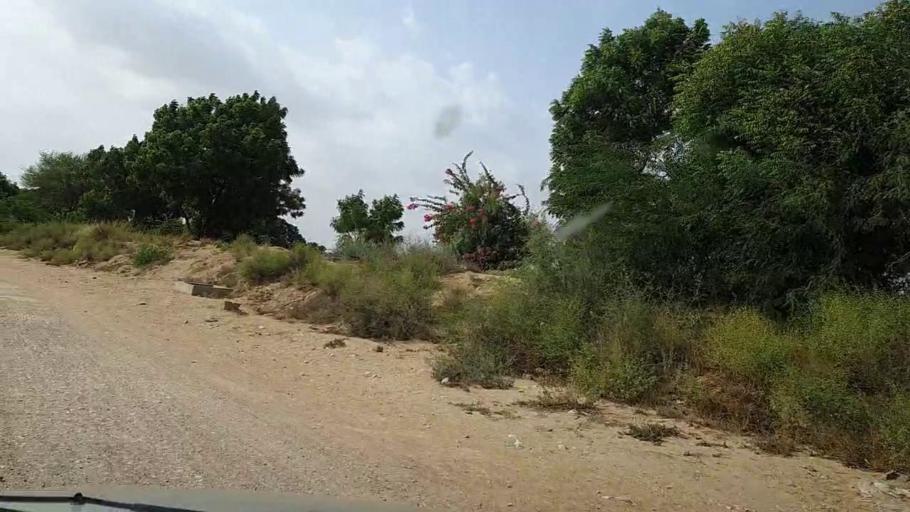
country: PK
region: Sindh
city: Kotri
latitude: 25.2397
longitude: 68.2663
